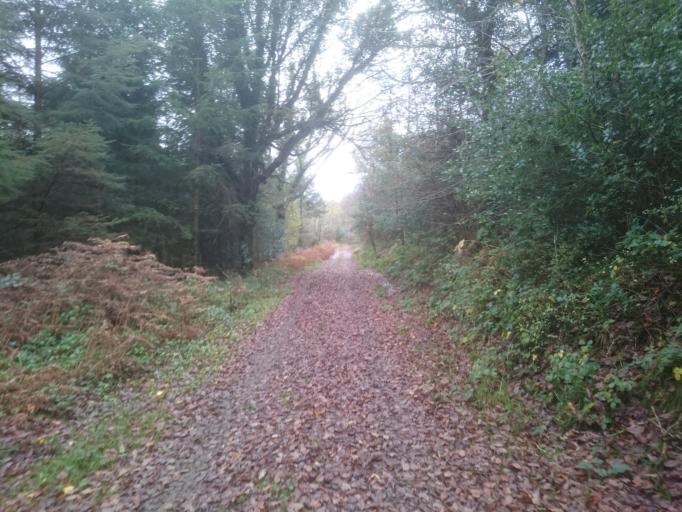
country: IE
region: Leinster
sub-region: Kilkenny
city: Thomastown
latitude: 52.4680
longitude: -7.0513
